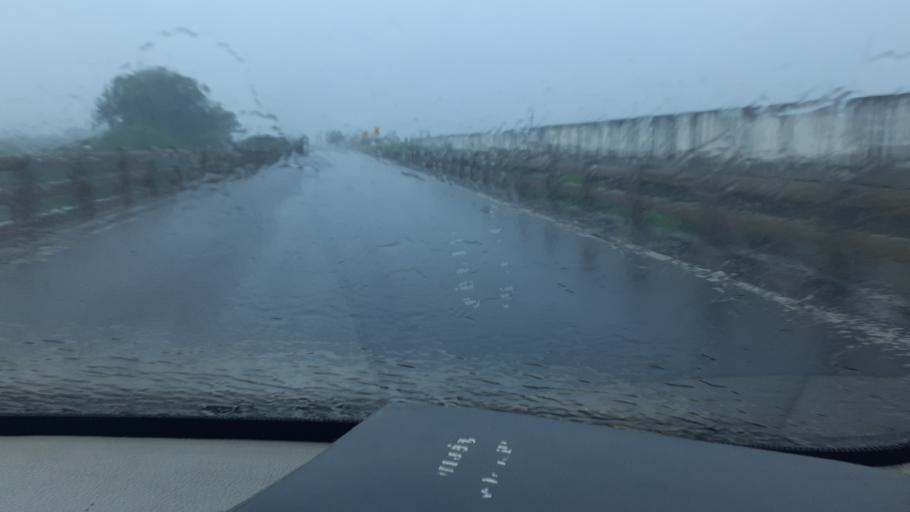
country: IN
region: Tamil Nadu
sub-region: Virudhunagar
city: Sattur
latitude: 9.4373
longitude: 77.9222
